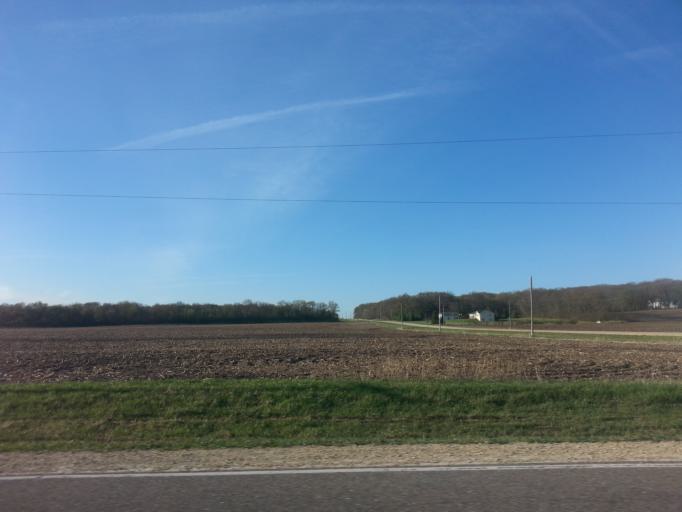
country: US
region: Minnesota
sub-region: Rice County
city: Northfield
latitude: 44.5436
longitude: -93.1172
